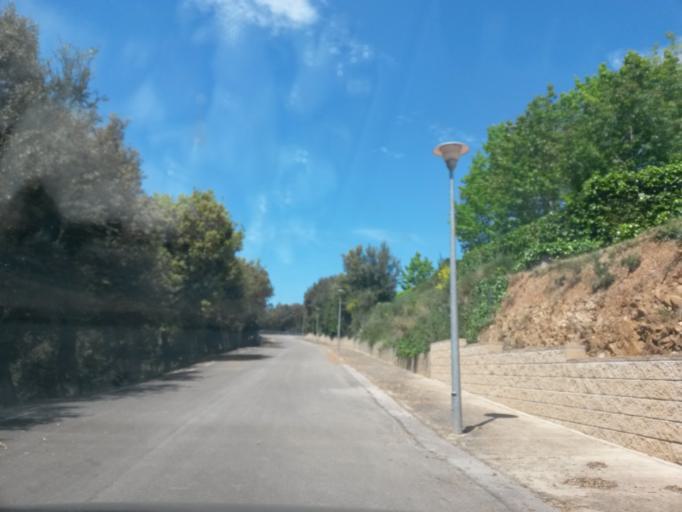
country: ES
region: Catalonia
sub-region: Provincia de Girona
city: Vilablareix
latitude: 41.9594
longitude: 2.7612
